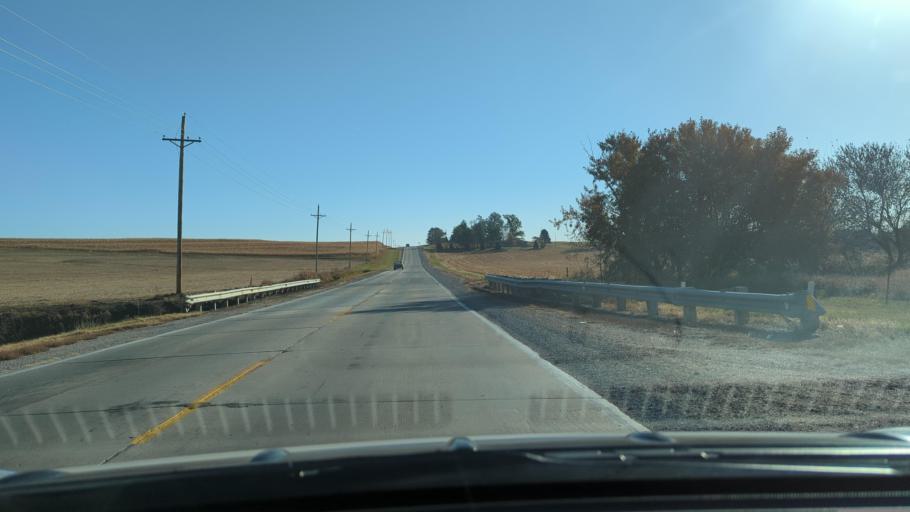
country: US
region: Nebraska
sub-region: Sarpy County
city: Papillion
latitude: 41.0925
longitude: -96.0372
